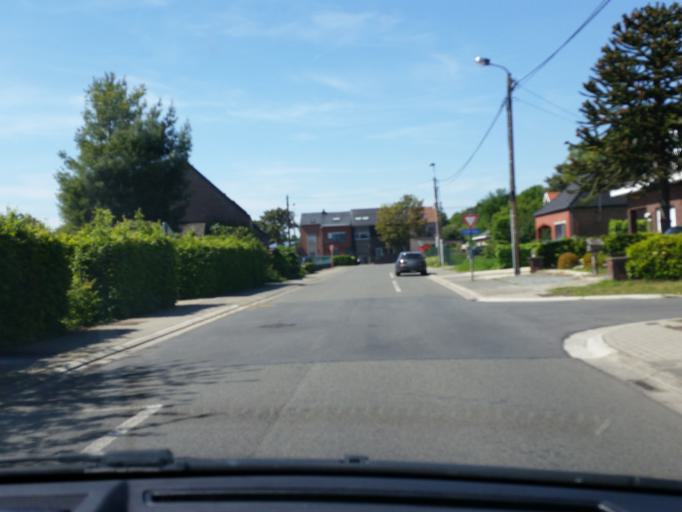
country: BE
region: Flanders
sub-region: Provincie Antwerpen
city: Bonheiden
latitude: 51.0202
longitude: 4.5389
